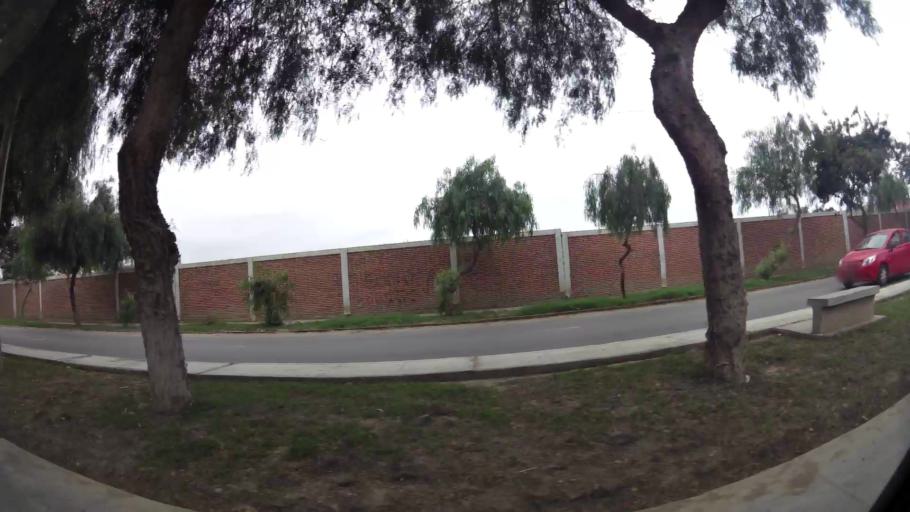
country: PE
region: La Libertad
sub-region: Provincia de Trujillo
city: Trujillo
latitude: -8.1153
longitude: -79.0432
